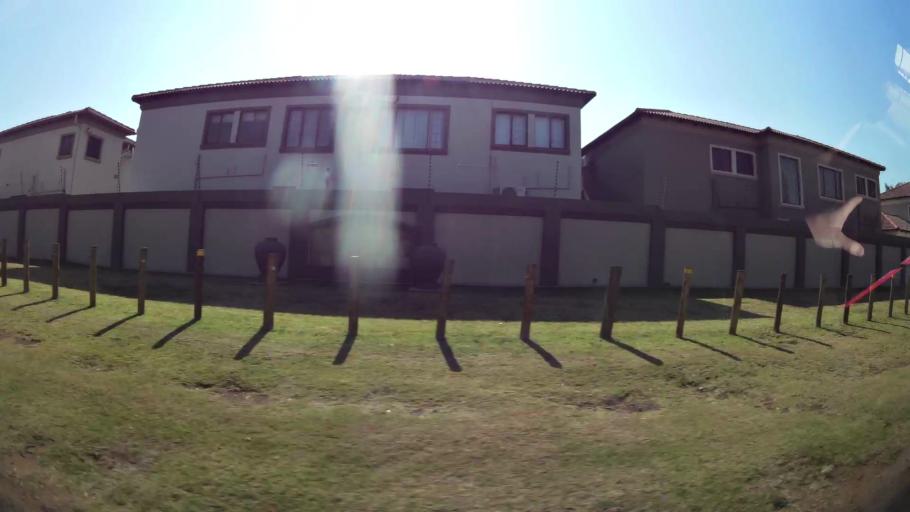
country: ZA
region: Gauteng
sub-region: Ekurhuleni Metropolitan Municipality
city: Boksburg
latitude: -26.1679
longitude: 28.2619
